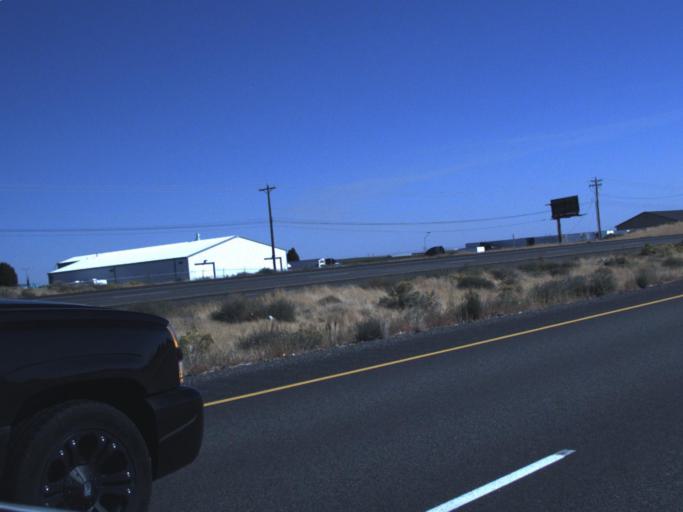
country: US
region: Washington
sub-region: Franklin County
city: Pasco
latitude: 46.2490
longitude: -119.0711
